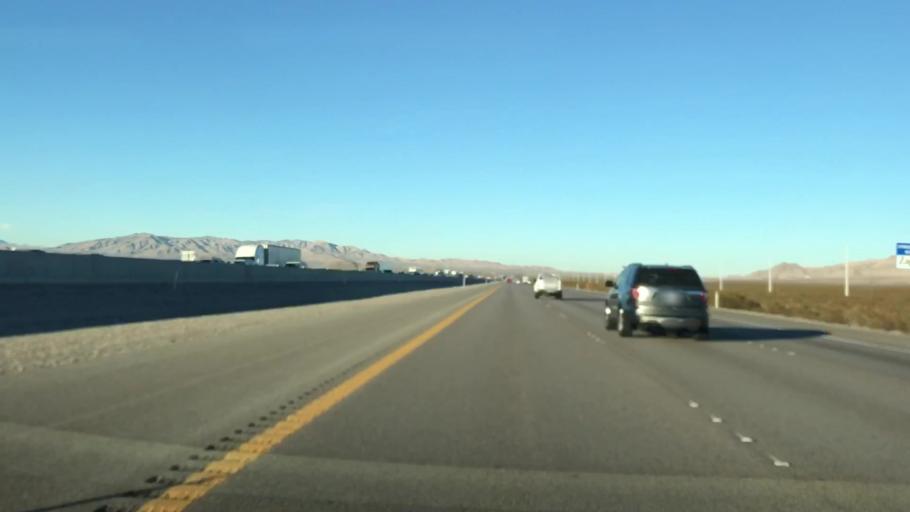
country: US
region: Nevada
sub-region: Clark County
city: Sandy Valley
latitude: 35.6913
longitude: -115.3733
